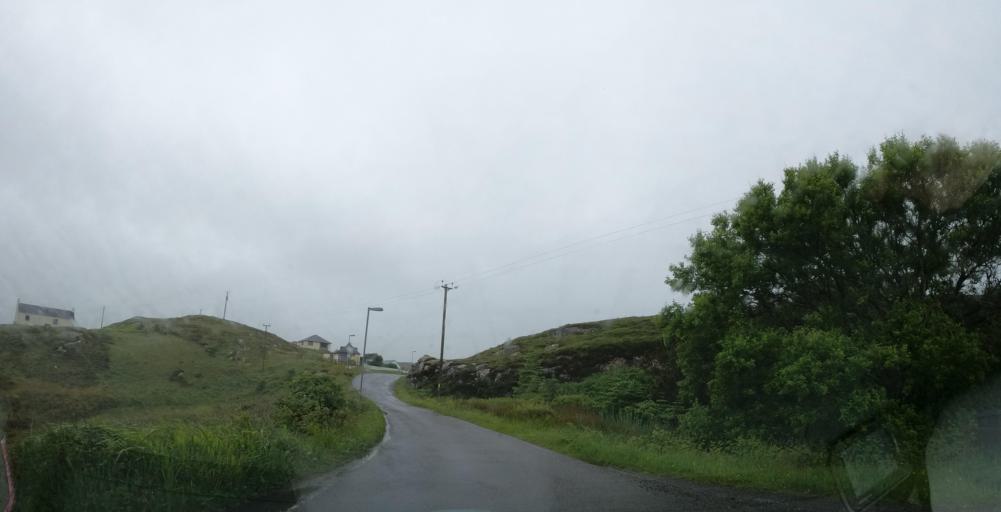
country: GB
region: Scotland
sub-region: Eilean Siar
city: Barra
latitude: 56.9972
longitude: -7.4196
